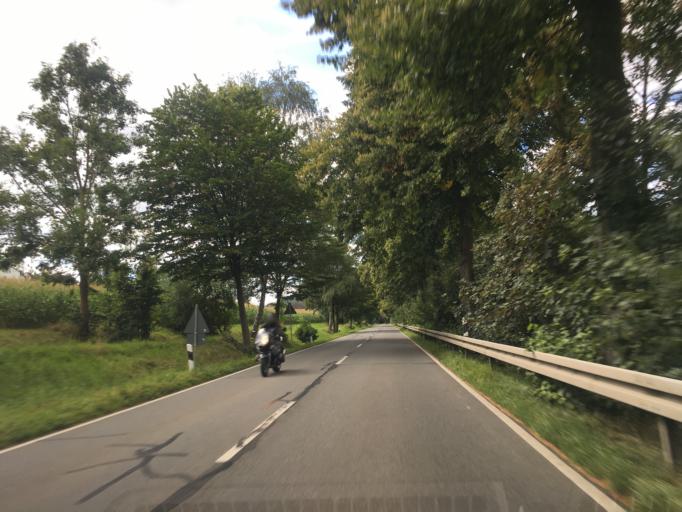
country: DE
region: Lower Saxony
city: Vahlbruch
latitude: 51.9909
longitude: 9.3289
